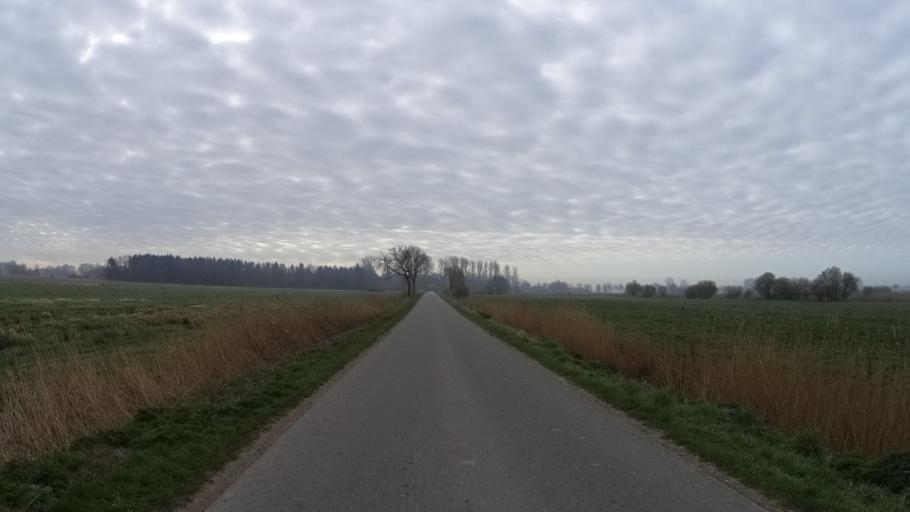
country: DE
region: Lower Saxony
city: Upgant-Schott
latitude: 53.4536
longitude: 7.3301
